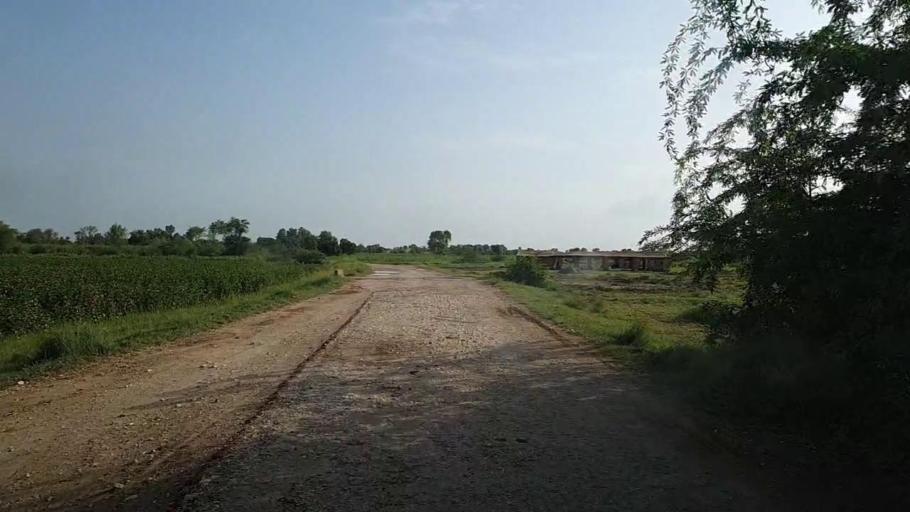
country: PK
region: Sindh
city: Pad Idan
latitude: 26.8115
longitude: 68.2352
